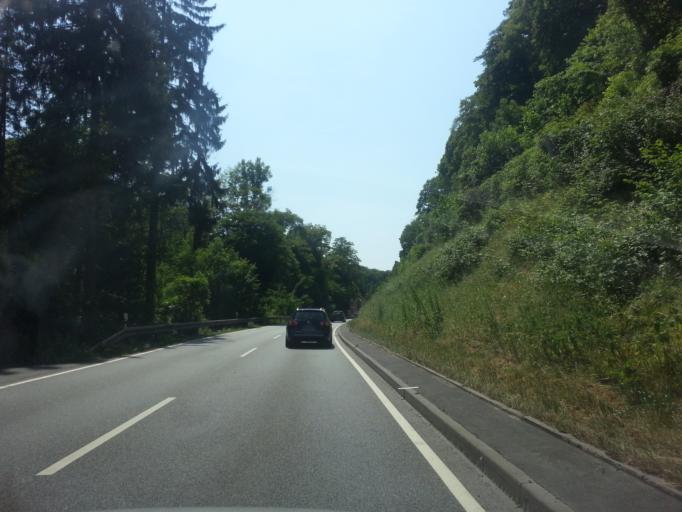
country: DE
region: Hesse
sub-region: Regierungsbezirk Darmstadt
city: Seeheim-Jugenheim
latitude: 49.8171
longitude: 8.6758
